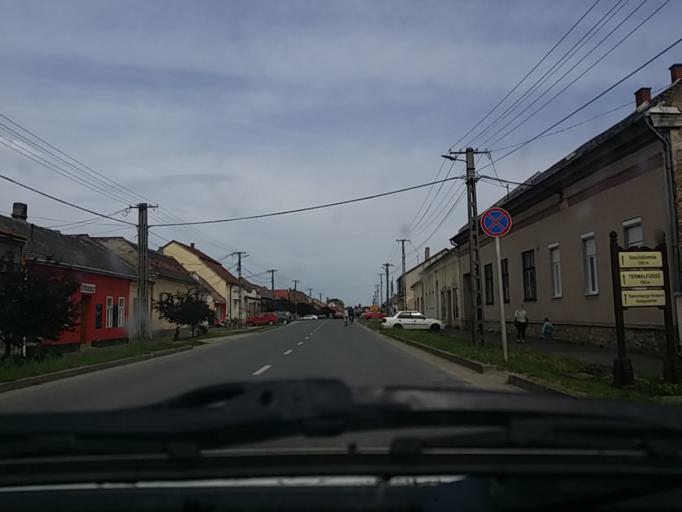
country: HU
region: Baranya
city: Sellye
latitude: 45.8723
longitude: 17.8485
